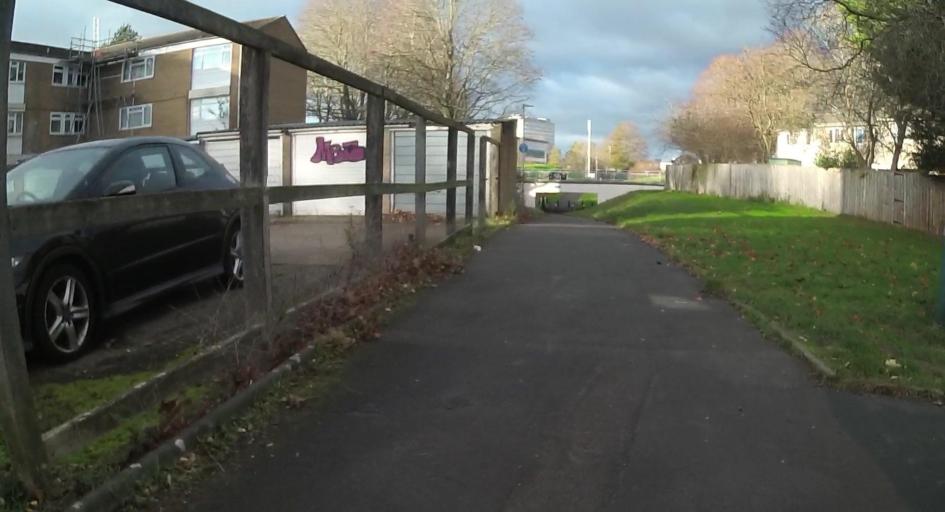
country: GB
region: England
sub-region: Bracknell Forest
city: Bracknell
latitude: 51.4032
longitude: -0.7720
